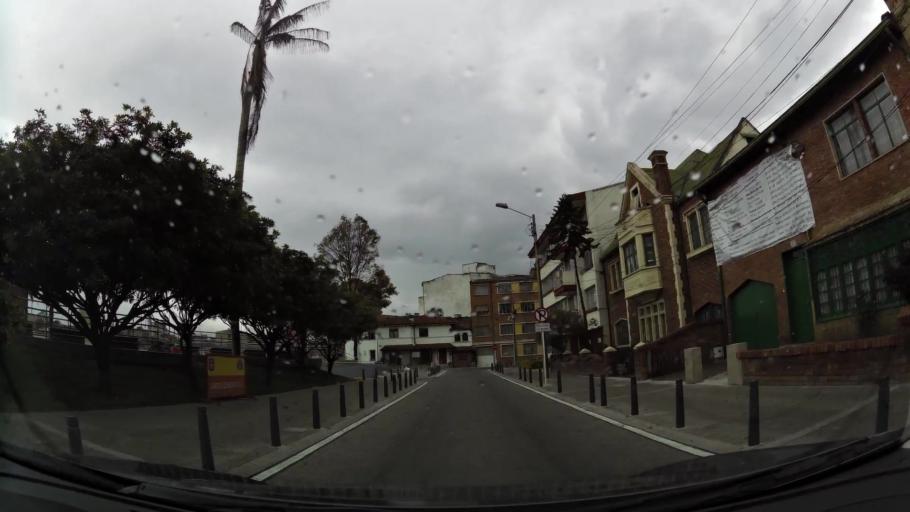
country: CO
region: Bogota D.C.
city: Bogota
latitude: 4.6252
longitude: -74.0783
